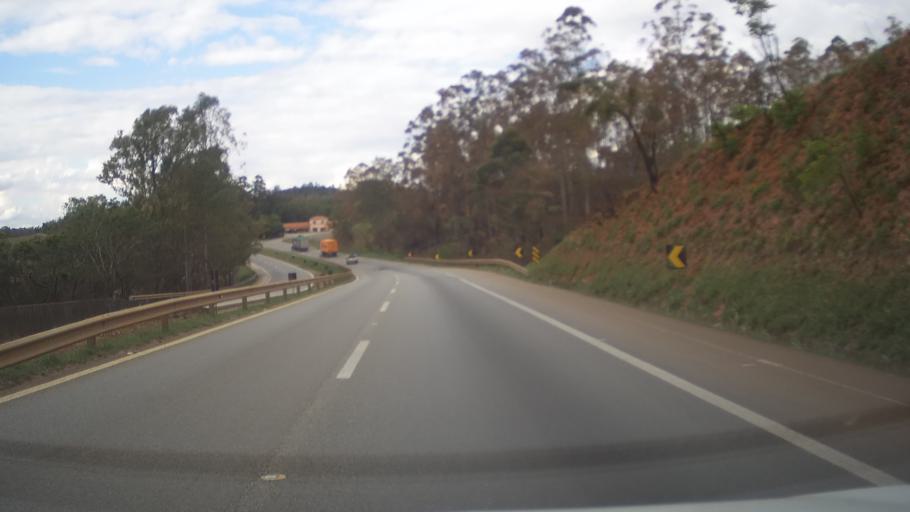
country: BR
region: Minas Gerais
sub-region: Itauna
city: Itauna
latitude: -20.2969
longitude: -44.4389
